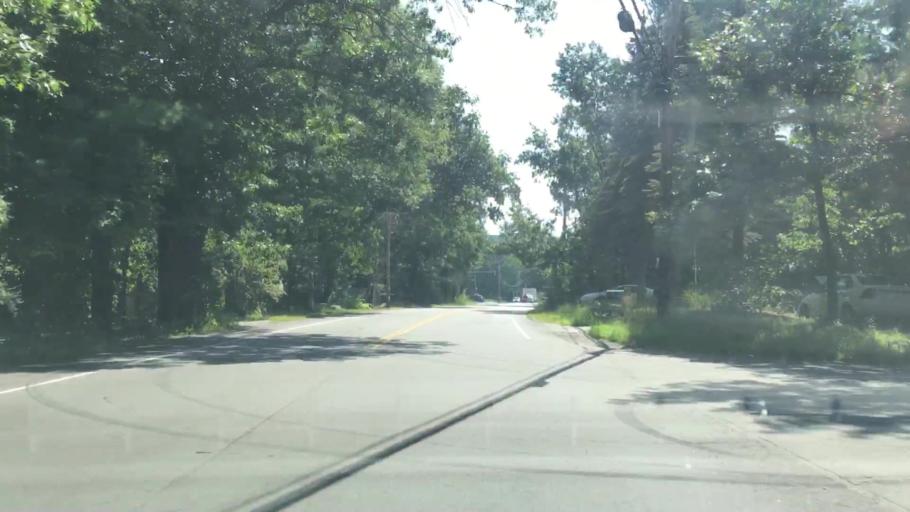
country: US
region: New Hampshire
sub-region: Rockingham County
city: Hampstead
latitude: 42.8536
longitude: -71.2177
